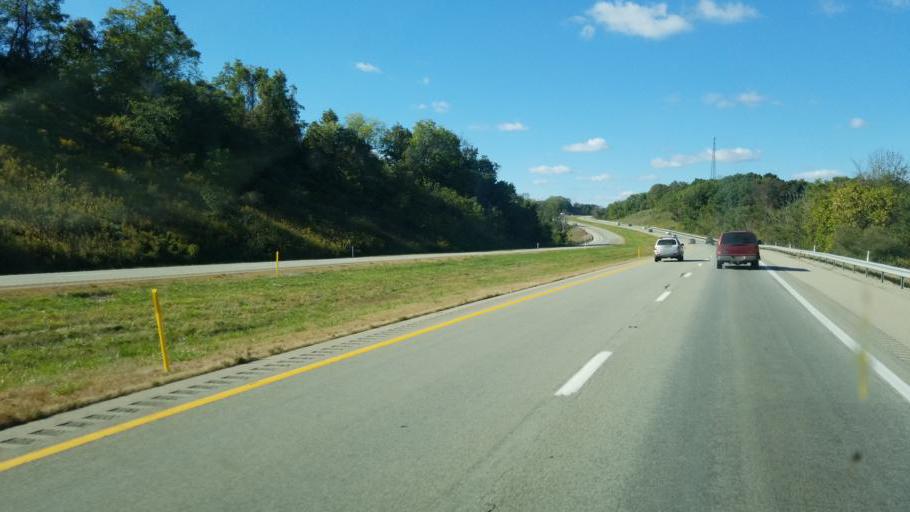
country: US
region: Pennsylvania
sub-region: Greene County
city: Morrisville
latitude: 39.8475
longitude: -80.1158
